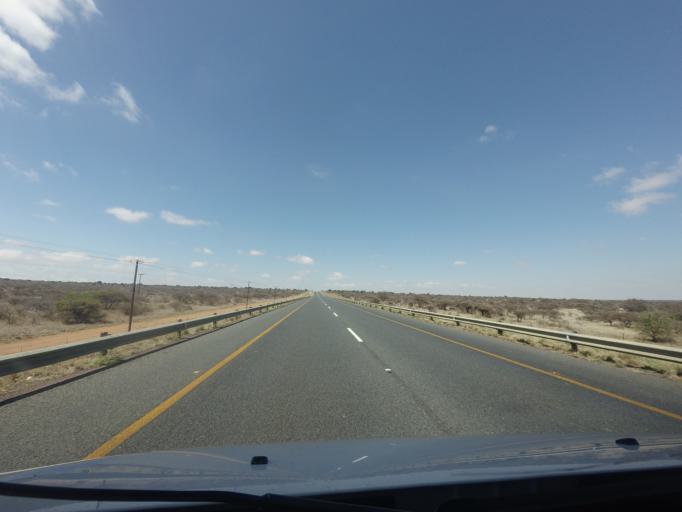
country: ZA
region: Limpopo
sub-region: Vhembe District Municipality
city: Louis Trichardt
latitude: -23.3935
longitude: 29.7620
